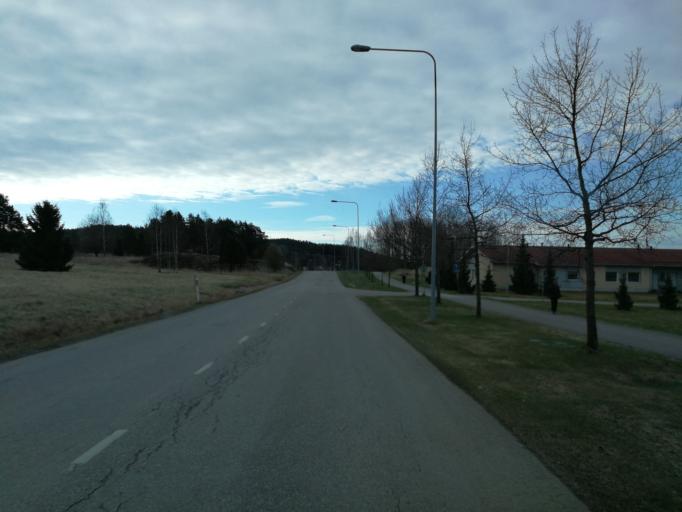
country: FI
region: Varsinais-Suomi
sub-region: Salo
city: Salo
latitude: 60.3772
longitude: 23.1620
